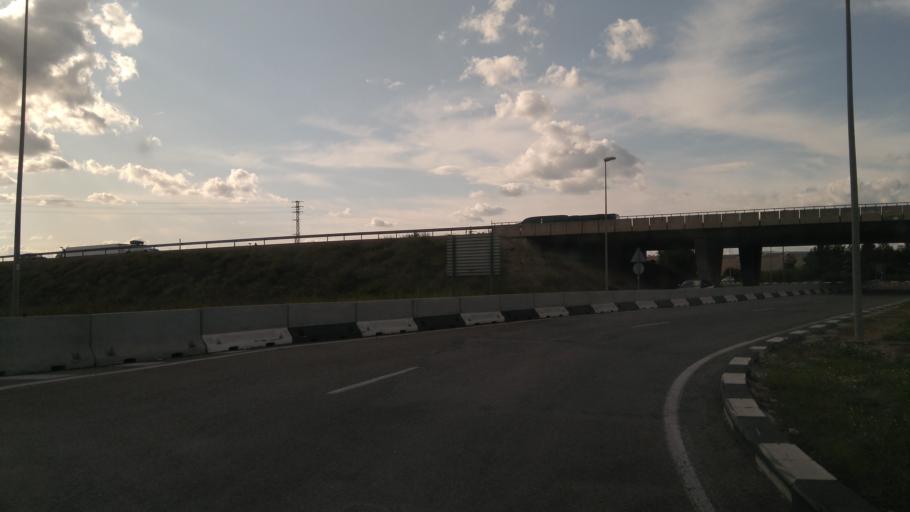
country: ES
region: Valencia
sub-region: Provincia de Valencia
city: L'Alcudia
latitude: 39.1932
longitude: -0.4945
